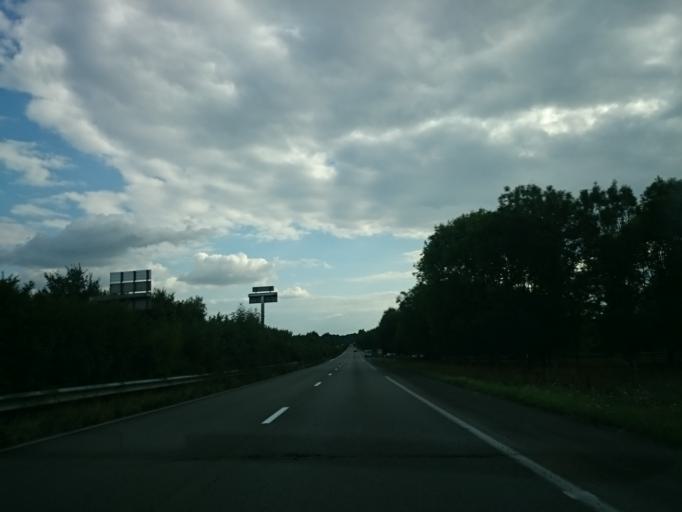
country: FR
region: Pays de la Loire
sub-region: Departement de la Loire-Atlantique
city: Nozay
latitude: 47.5767
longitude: -1.6303
